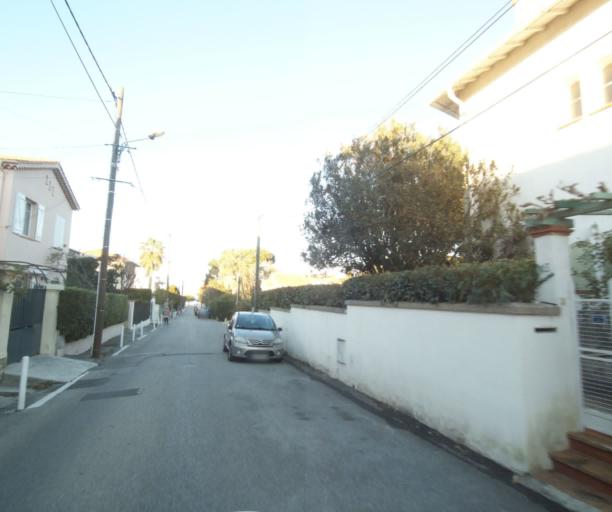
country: FR
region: Provence-Alpes-Cote d'Azur
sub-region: Departement des Alpes-Maritimes
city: Antibes
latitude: 43.5673
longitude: 7.1290
